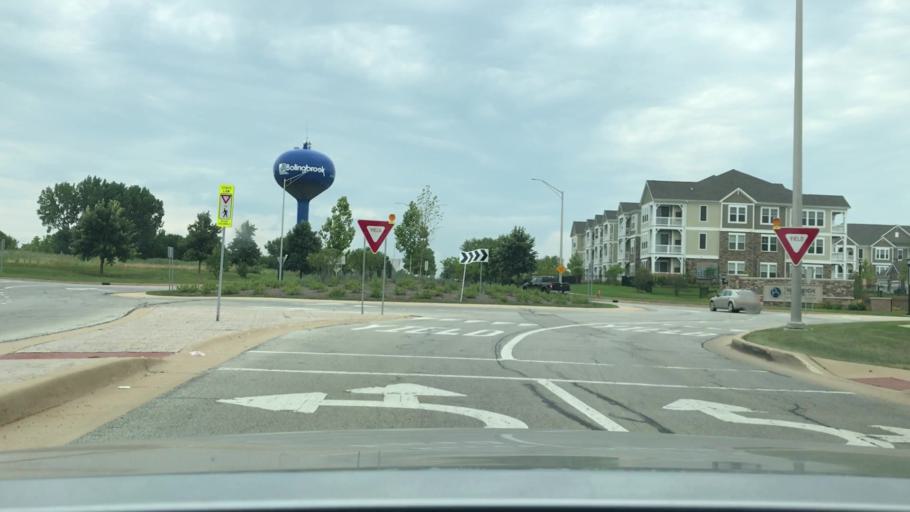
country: US
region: Illinois
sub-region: Will County
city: Bolingbrook
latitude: 41.7113
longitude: -88.0395
